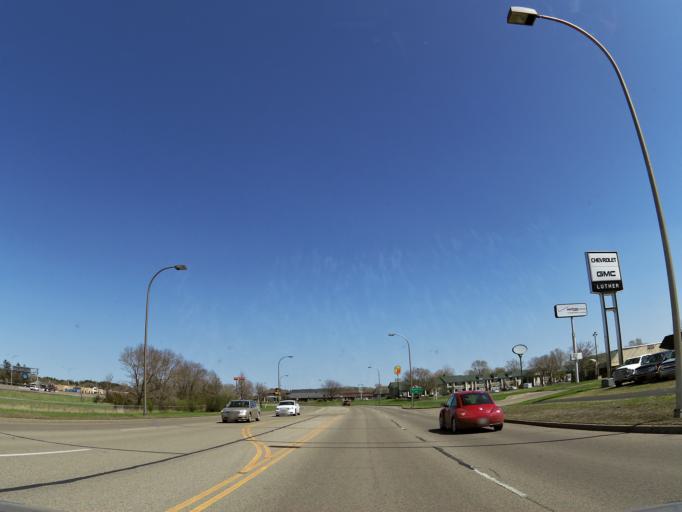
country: US
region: Wisconsin
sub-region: Saint Croix County
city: Hudson
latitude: 44.9618
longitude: -92.7412
